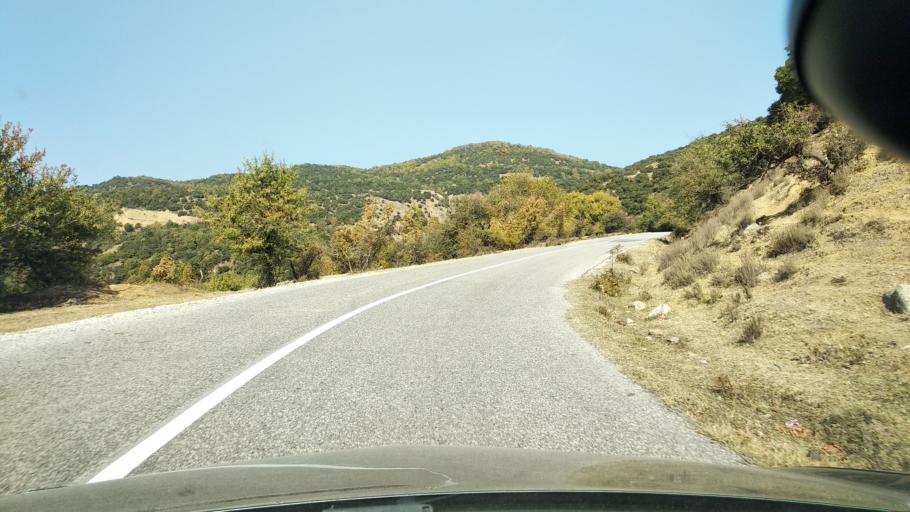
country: GR
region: Thessaly
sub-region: Trikala
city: Kalampaka
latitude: 39.7139
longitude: 21.6494
